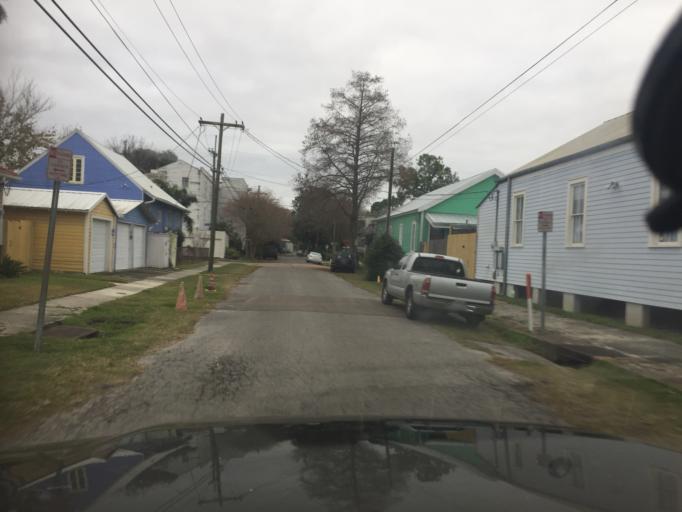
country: US
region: Louisiana
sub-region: Orleans Parish
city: New Orleans
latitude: 29.9809
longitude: -90.0797
